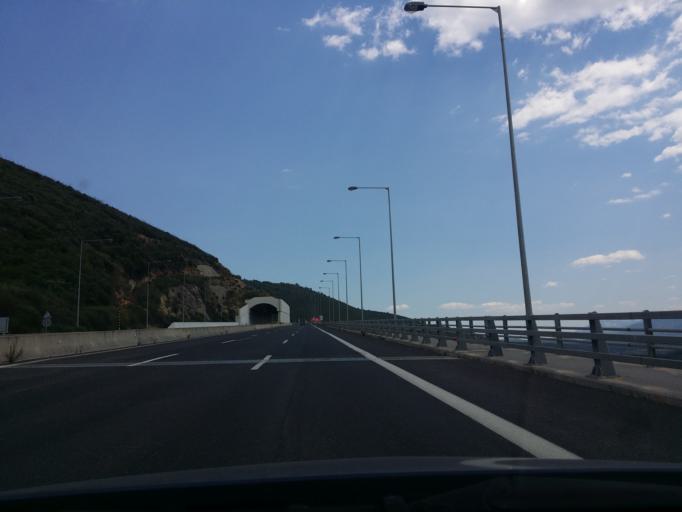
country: GR
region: Peloponnese
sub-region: Nomos Arkadias
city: Megalopoli
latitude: 37.3903
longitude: 22.1874
